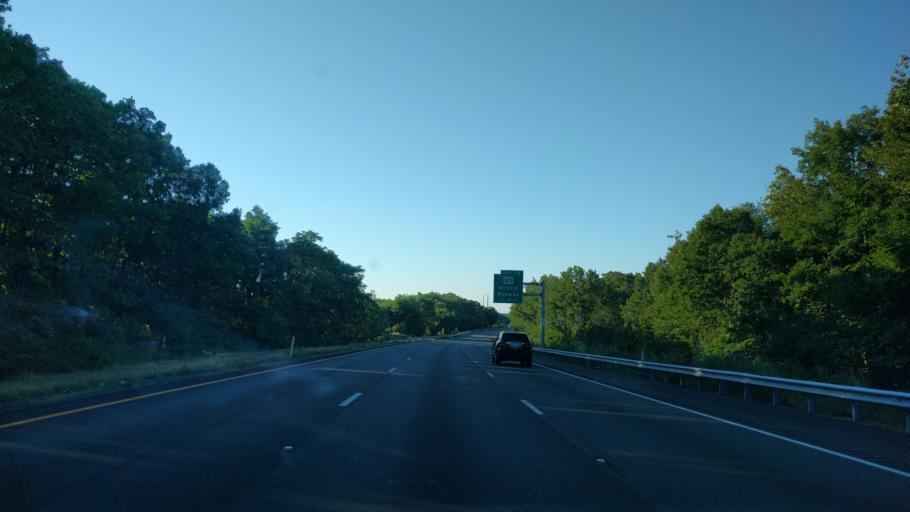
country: US
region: Massachusetts
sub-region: Worcester County
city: Milford
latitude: 42.1569
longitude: -71.4902
